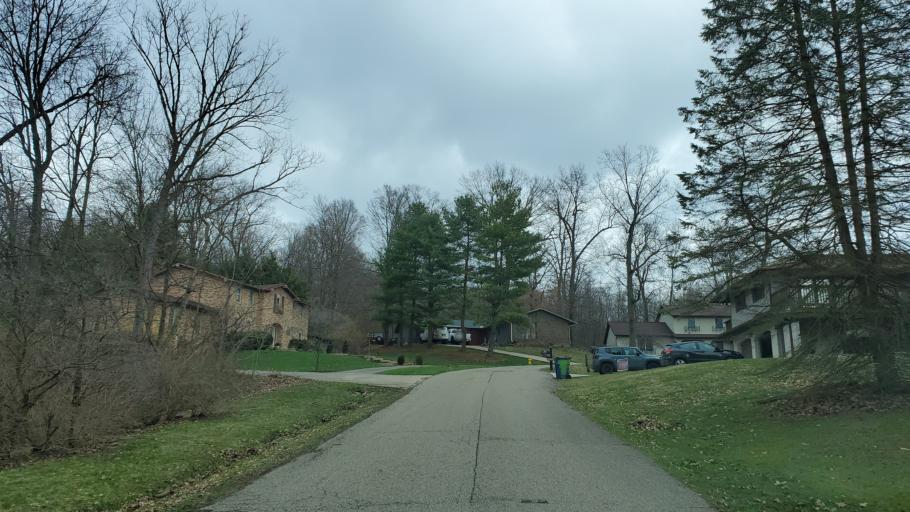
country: US
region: Ohio
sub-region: Licking County
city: Newark
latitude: 40.0230
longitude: -82.3786
